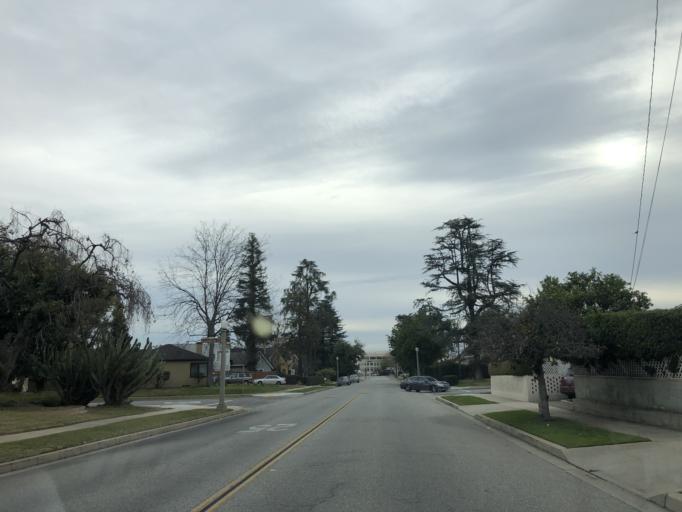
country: US
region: California
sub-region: Los Angeles County
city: San Gabriel
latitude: 34.1048
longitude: -118.1050
